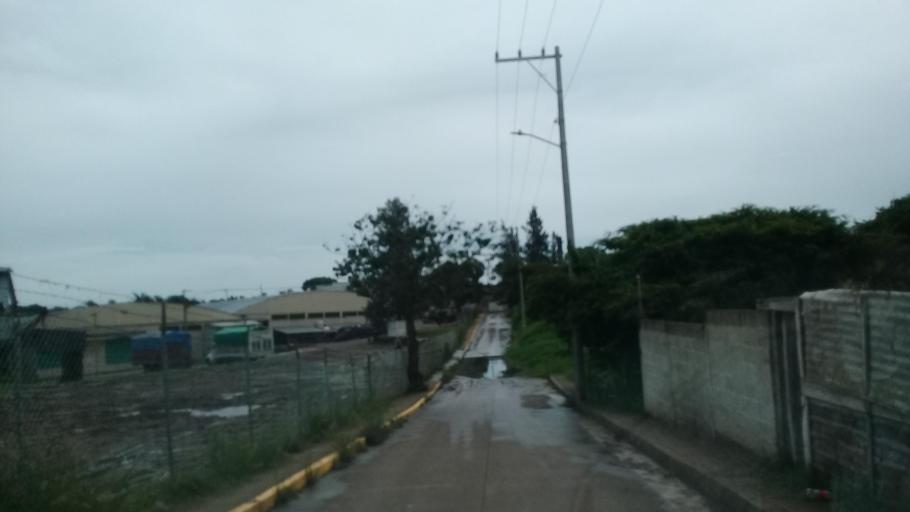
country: MX
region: Veracruz
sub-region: Emiliano Zapata
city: Dos Rios
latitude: 19.4815
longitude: -96.8000
